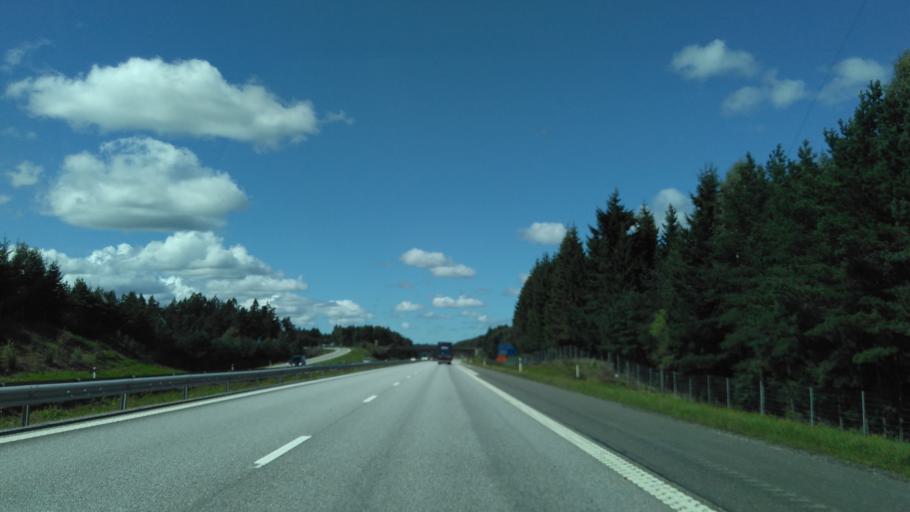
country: SE
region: Vaestra Goetaland
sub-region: Harryda Kommun
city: Hindas
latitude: 57.6731
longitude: 12.3603
